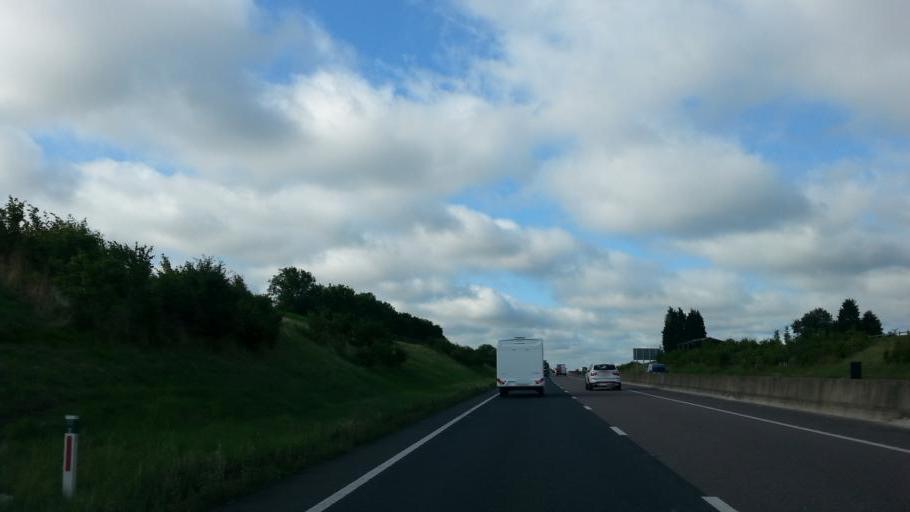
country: GB
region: England
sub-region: Nottinghamshire
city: East Bridgford
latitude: 52.9950
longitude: -0.9268
